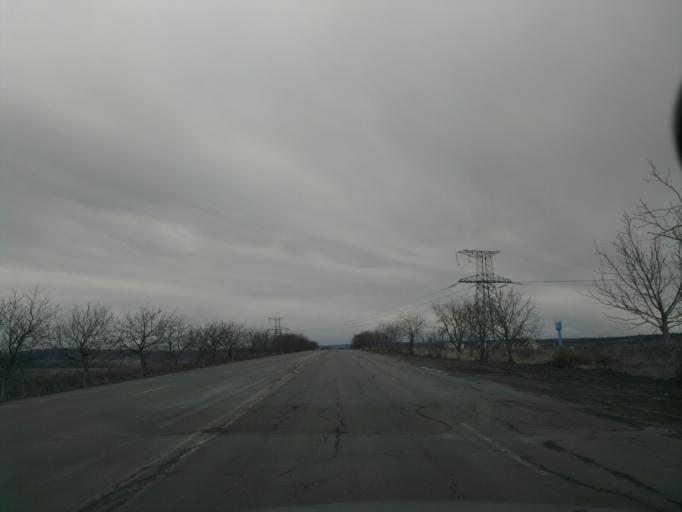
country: MD
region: Chisinau
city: Vatra
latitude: 47.0064
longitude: 28.7283
